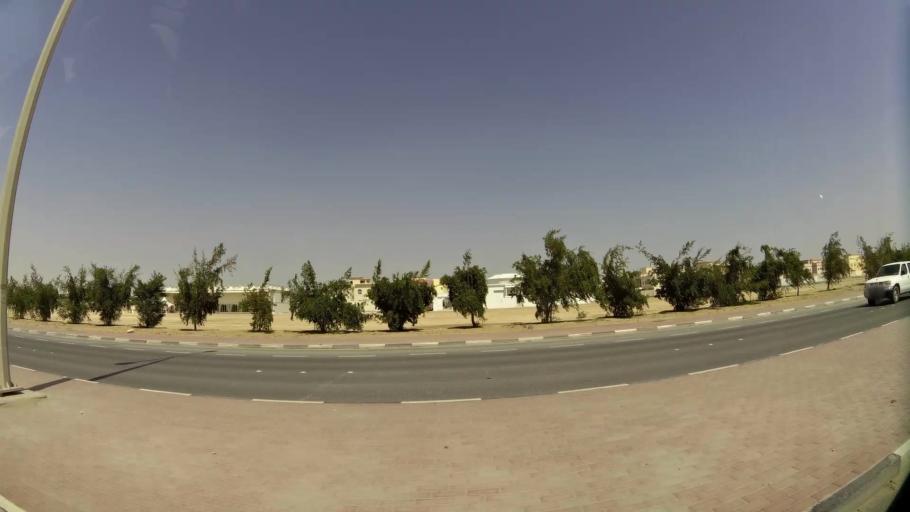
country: QA
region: Baladiyat Umm Salal
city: Umm Salal Muhammad
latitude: 25.3827
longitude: 51.4265
